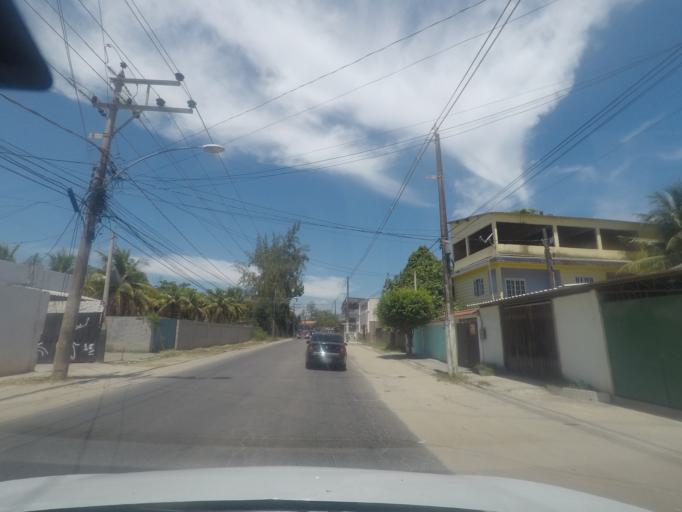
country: BR
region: Rio de Janeiro
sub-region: Itaguai
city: Itaguai
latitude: -22.9777
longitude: -43.6745
